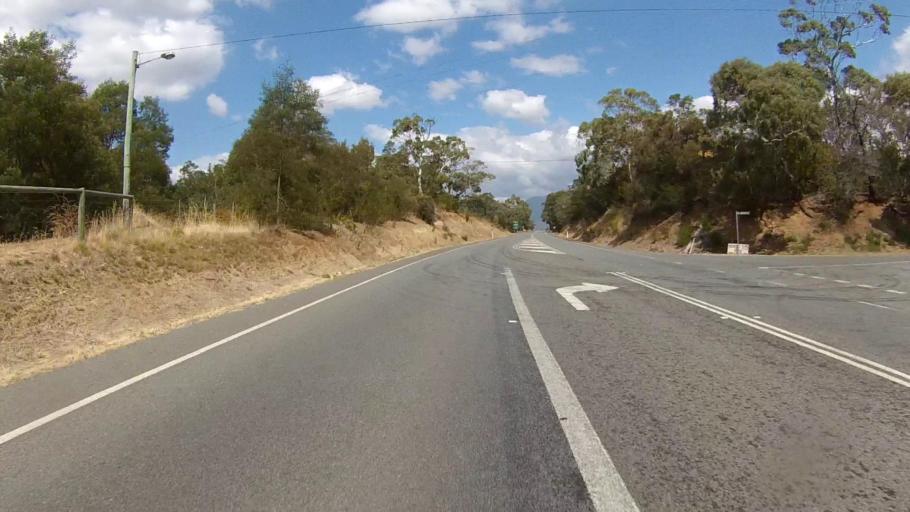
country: AU
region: Tasmania
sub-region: Brighton
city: Old Beach
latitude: -42.7667
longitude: 147.2701
